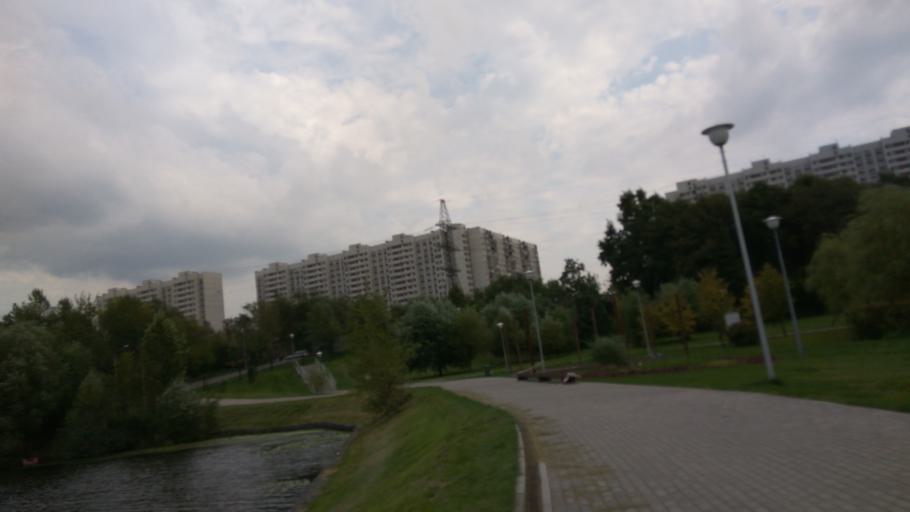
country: RU
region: Moscow
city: Mar'ino
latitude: 55.6382
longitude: 37.7388
